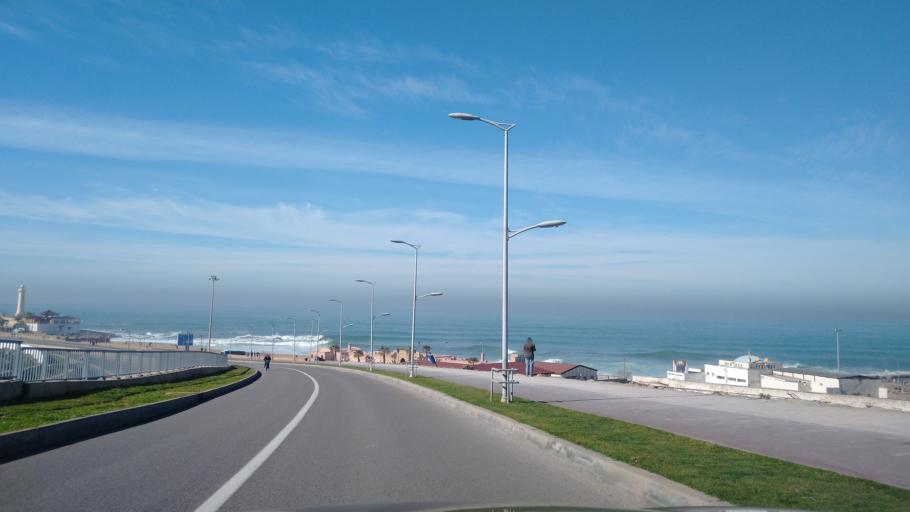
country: MA
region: Rabat-Sale-Zemmour-Zaer
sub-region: Rabat
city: Rabat
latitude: 34.0313
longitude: -6.8382
